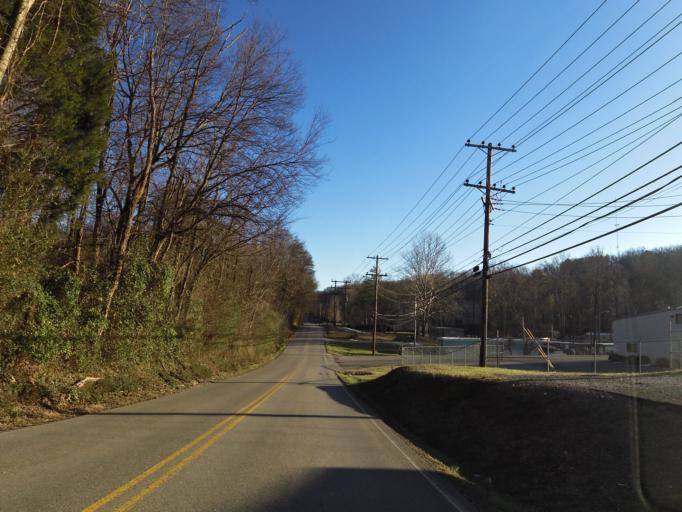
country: US
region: Tennessee
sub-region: Knox County
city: Farragut
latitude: 35.8917
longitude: -84.1353
